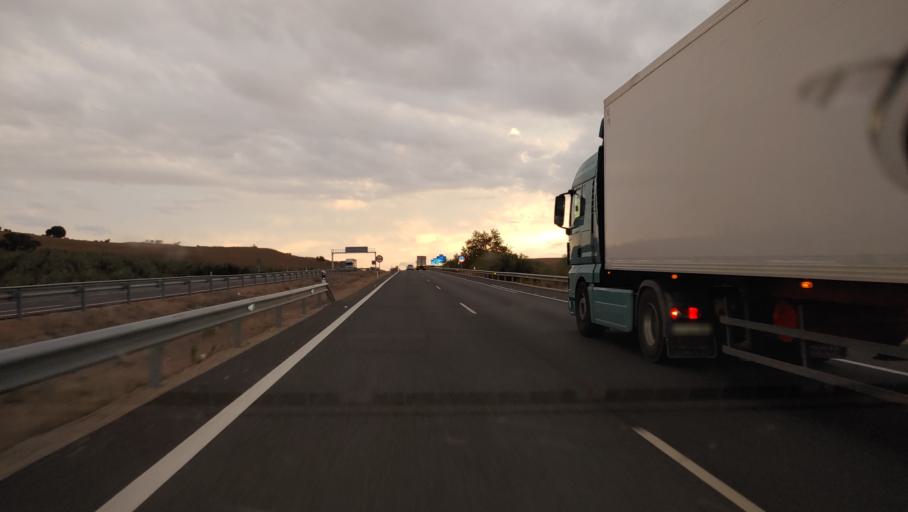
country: ES
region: Andalusia
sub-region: Provincia de Jaen
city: Mengibar
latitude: 38.0179
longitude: -3.7820
